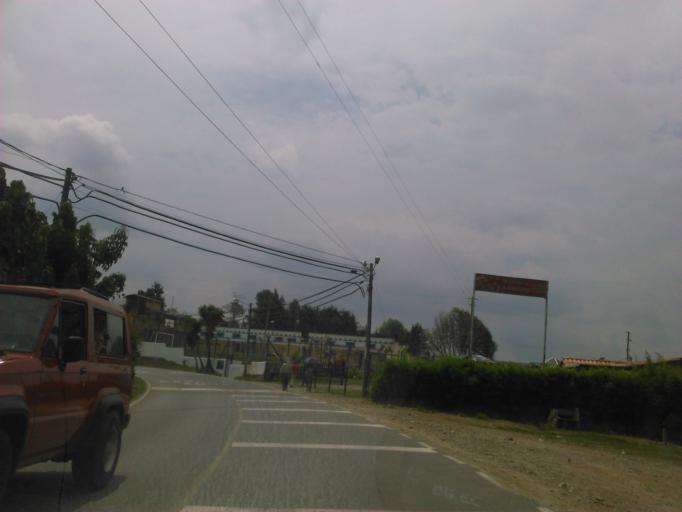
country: CO
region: Antioquia
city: San Vicente
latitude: 6.2329
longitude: -75.3846
